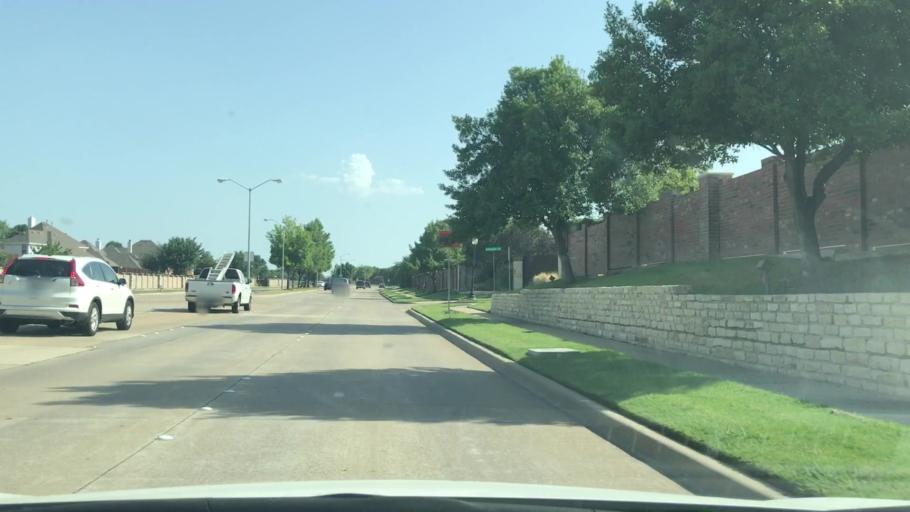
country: US
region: Texas
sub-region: Collin County
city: Allen
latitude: 33.0915
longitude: -96.7491
